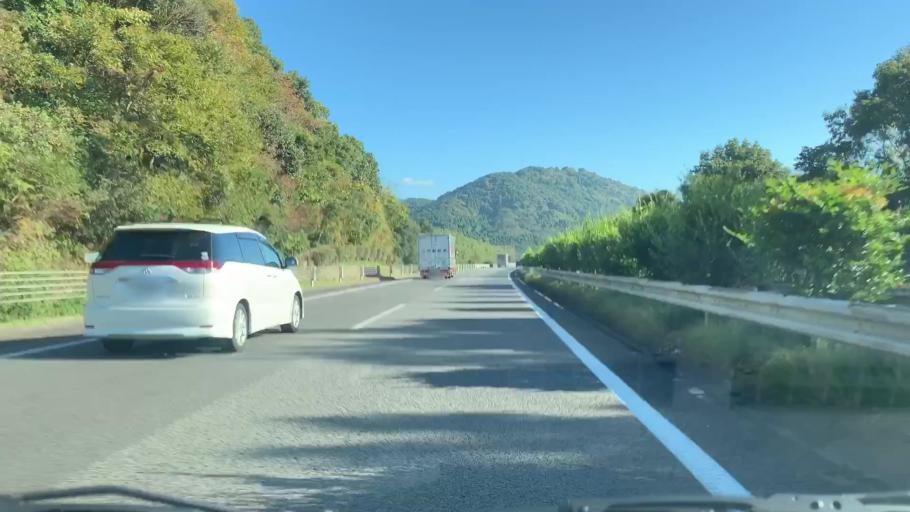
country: JP
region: Saga Prefecture
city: Takeocho-takeo
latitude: 33.2653
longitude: 130.0864
